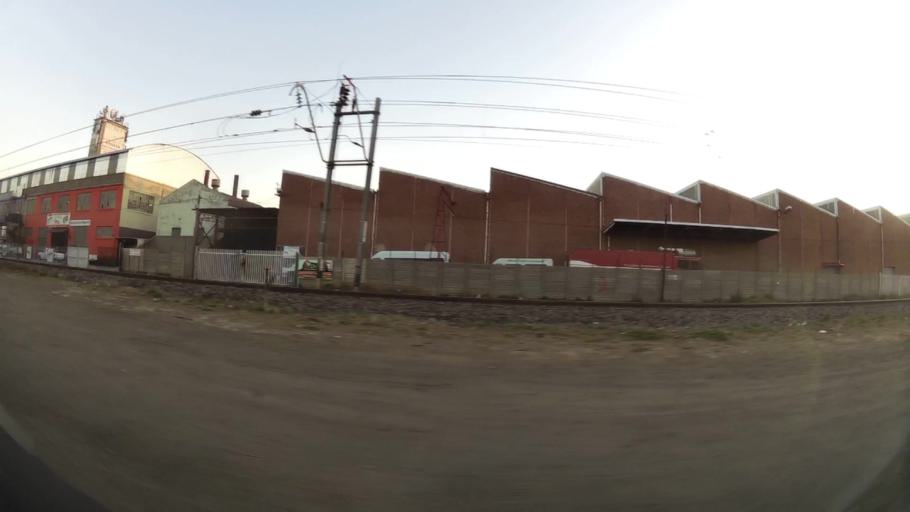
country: ZA
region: North-West
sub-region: Bojanala Platinum District Municipality
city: Rustenburg
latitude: -25.6620
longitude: 27.2494
